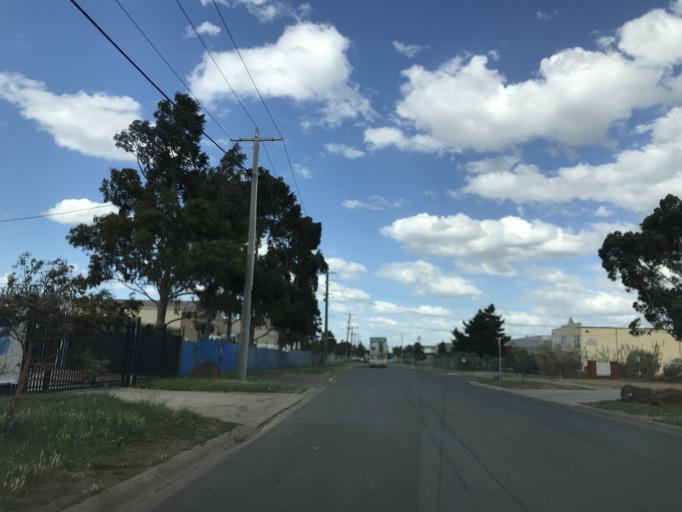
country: AU
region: Victoria
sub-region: Brimbank
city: Sunshine West
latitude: -37.8105
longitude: 144.8121
